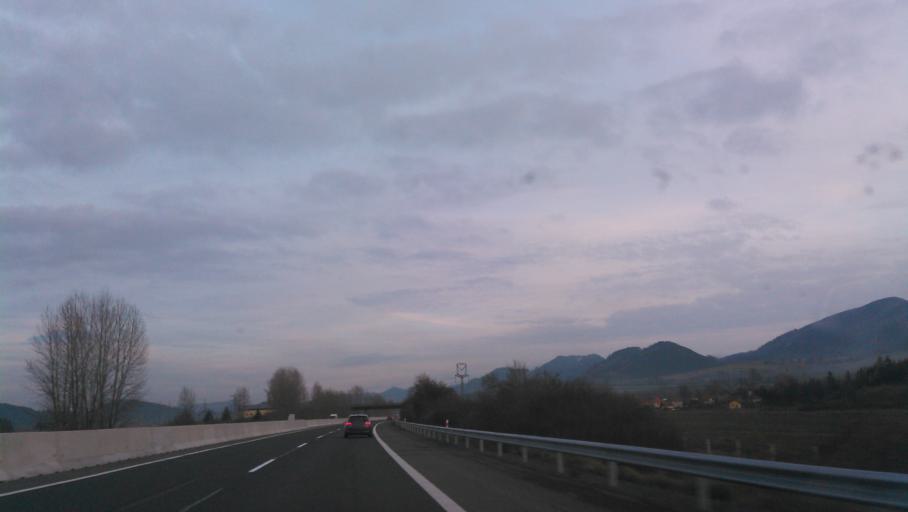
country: SK
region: Zilinsky
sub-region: Okres Liptovsky Mikulas
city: Liptovsky Mikulas
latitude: 49.0661
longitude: 19.6423
